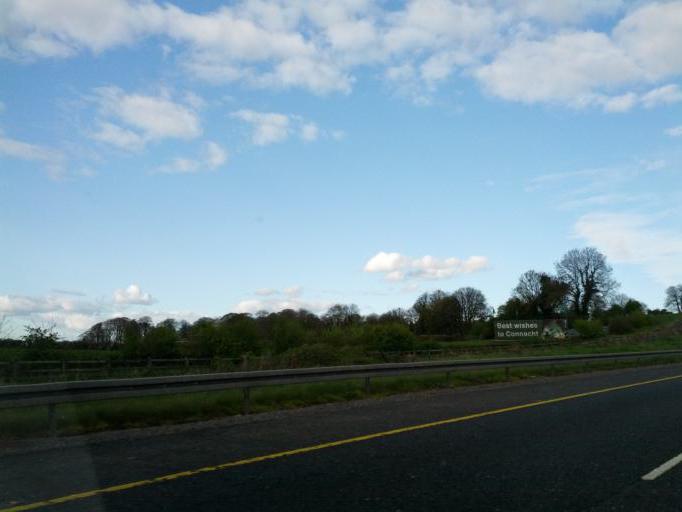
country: IE
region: Leinster
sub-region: An Mhi
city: Enfield
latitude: 53.4114
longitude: -6.7709
